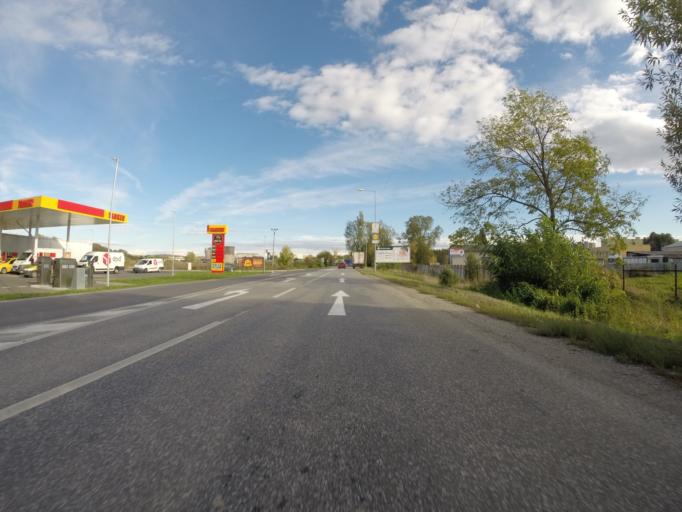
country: SK
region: Banskobystricky
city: Rimavska Sobota
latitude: 48.3881
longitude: 19.9980
